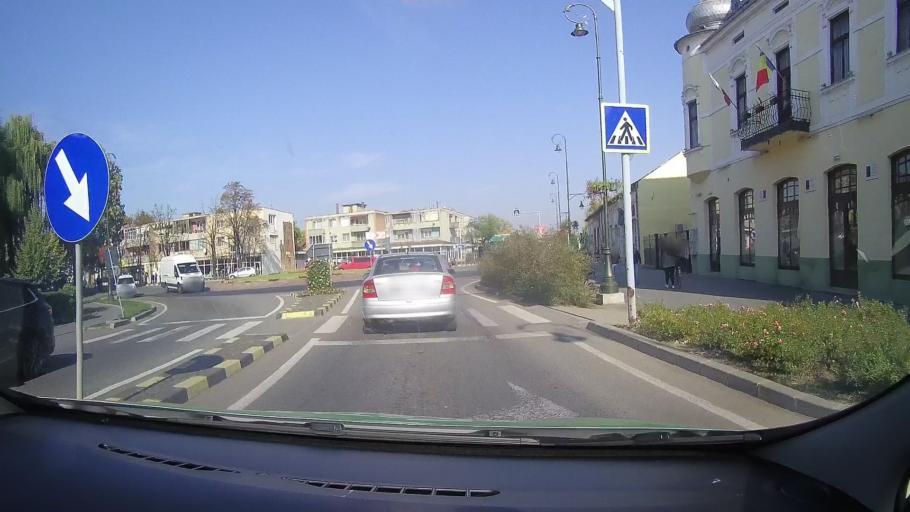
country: RO
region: Bihor
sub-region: Municipiul Salonta
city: Salonta
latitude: 46.8020
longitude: 21.6628
